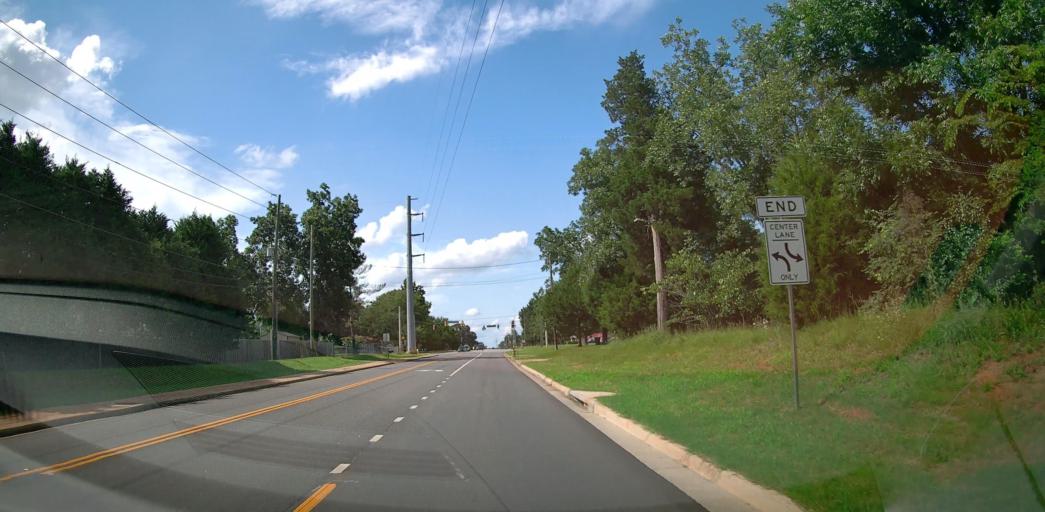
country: US
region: Georgia
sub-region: Houston County
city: Perry
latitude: 32.5295
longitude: -83.6910
